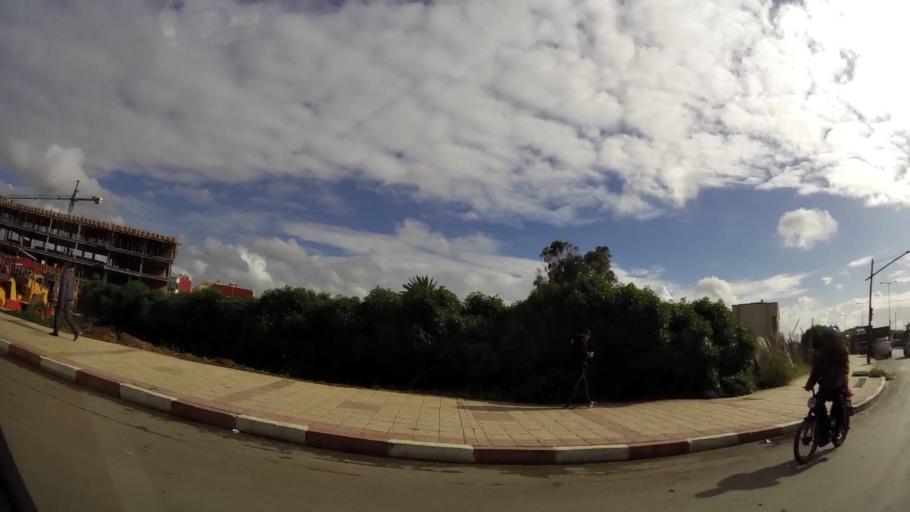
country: MA
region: Grand Casablanca
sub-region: Mohammedia
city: Mohammedia
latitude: 33.6911
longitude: -7.3724
